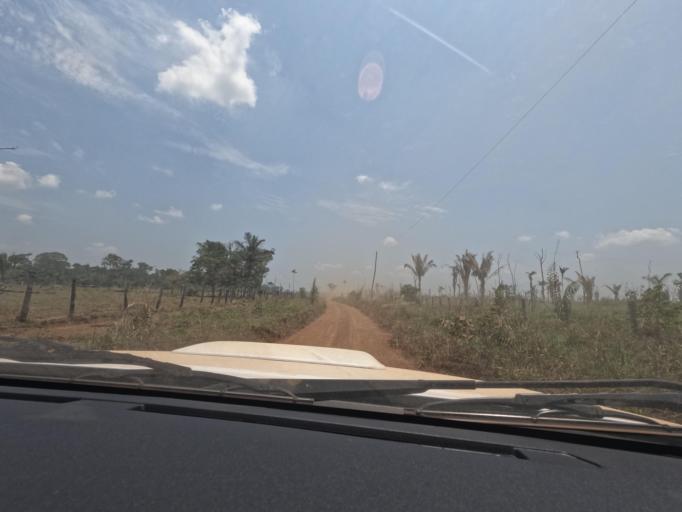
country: BR
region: Rondonia
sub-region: Porto Velho
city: Porto Velho
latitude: -8.6489
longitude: -64.1711
